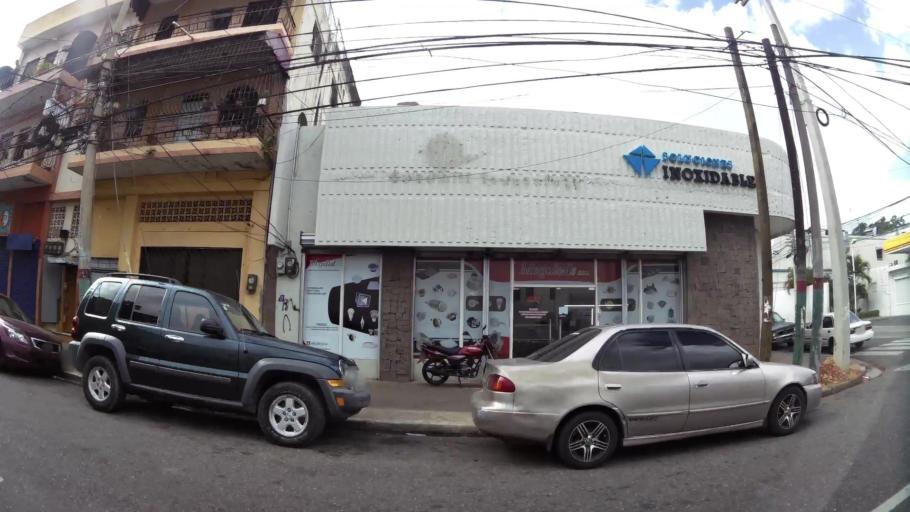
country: DO
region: Nacional
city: San Carlos
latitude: 18.4801
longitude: -69.9043
